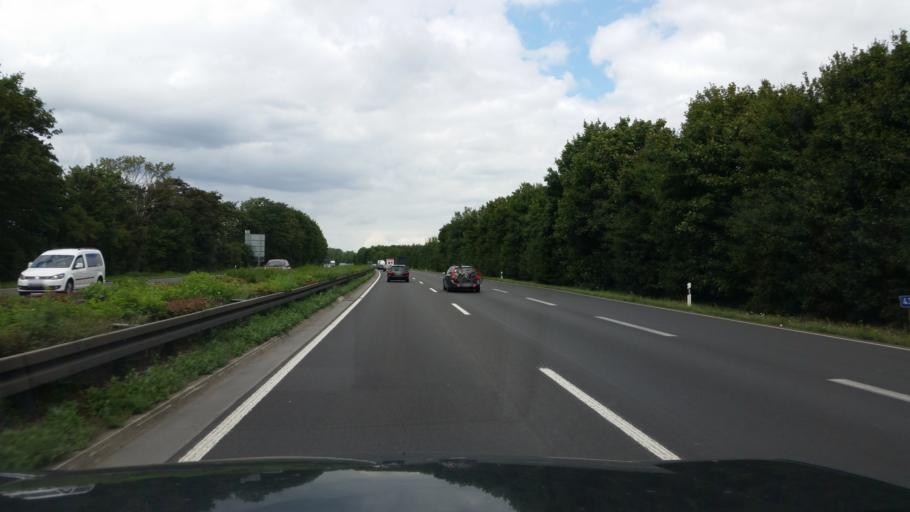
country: DE
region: North Rhine-Westphalia
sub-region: Regierungsbezirk Koln
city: Erftstadt
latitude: 50.8603
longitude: 6.8055
